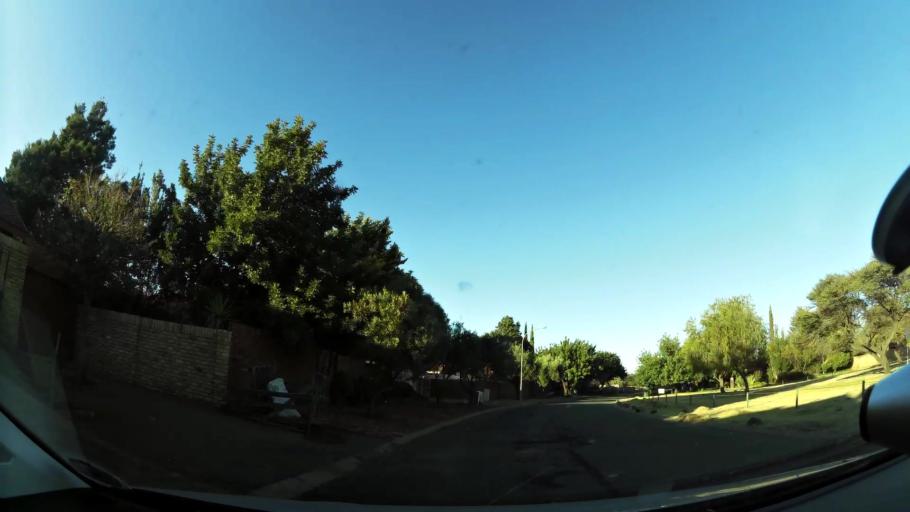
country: ZA
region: Northern Cape
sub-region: Frances Baard District Municipality
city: Kimberley
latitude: -28.7597
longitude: 24.7528
